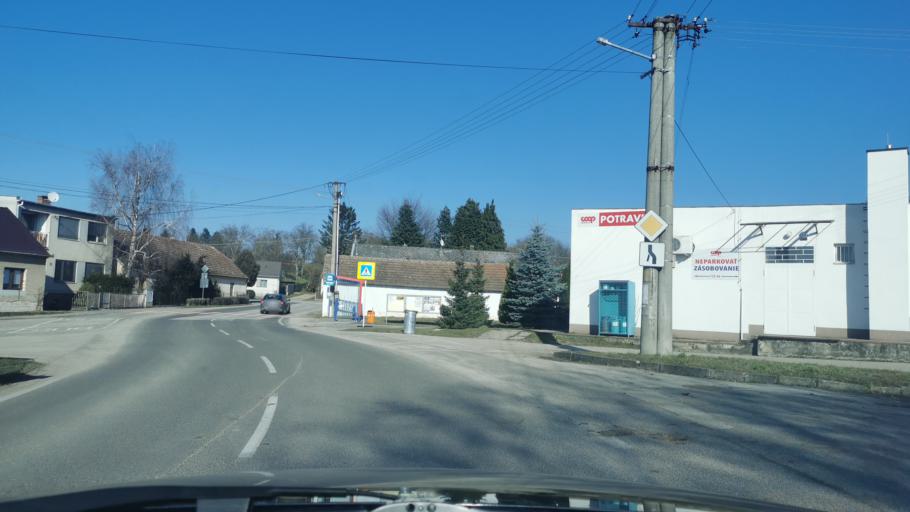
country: SK
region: Trnavsky
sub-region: Okres Senica
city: Senica
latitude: 48.6899
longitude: 17.4025
